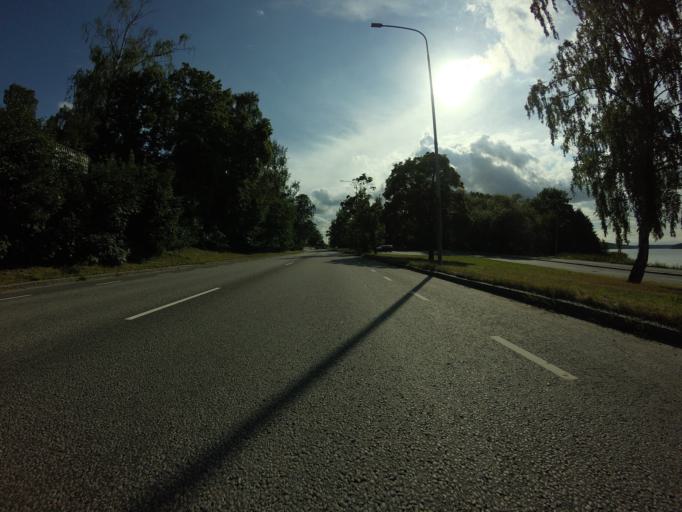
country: SE
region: Stockholm
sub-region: Lidingo
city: Lidingoe
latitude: 59.3679
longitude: 18.1184
